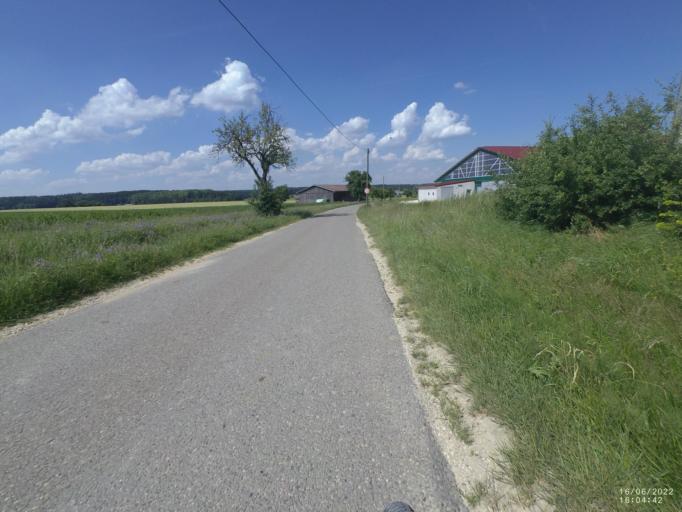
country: DE
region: Baden-Wuerttemberg
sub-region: Regierungsbezirk Stuttgart
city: Gerstetten
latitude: 48.6158
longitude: 10.0725
